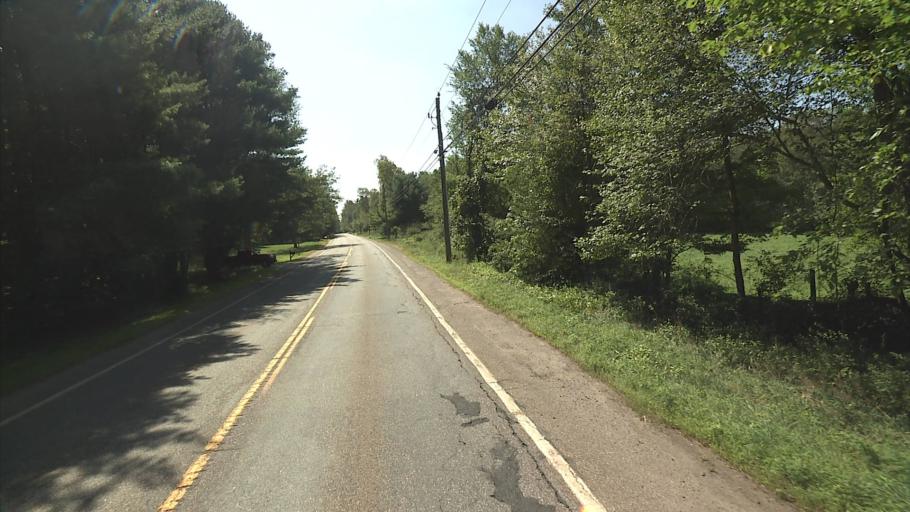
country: US
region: Connecticut
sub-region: Tolland County
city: Storrs
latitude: 41.8881
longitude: -72.1677
